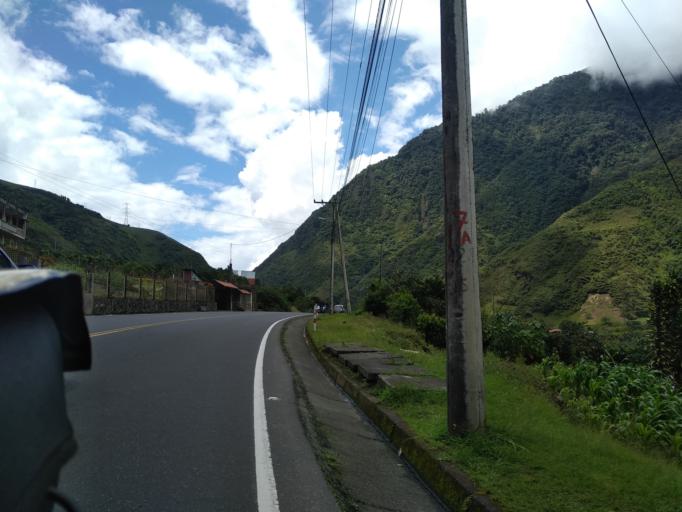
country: EC
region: Tungurahua
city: Banos
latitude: -1.3984
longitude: -78.3711
